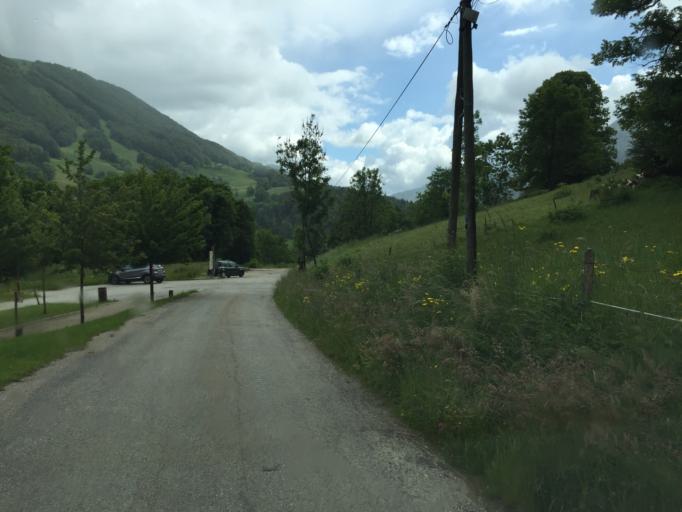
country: FR
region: Rhone-Alpes
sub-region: Departement de la Savoie
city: Cruet
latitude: 45.6147
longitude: 6.1110
